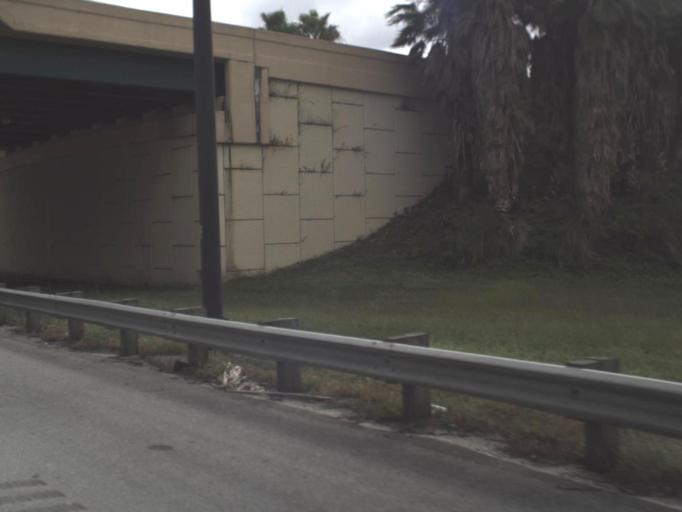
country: US
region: Florida
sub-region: Palm Beach County
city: Palm Beach Gardens
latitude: 26.8037
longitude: -80.1315
